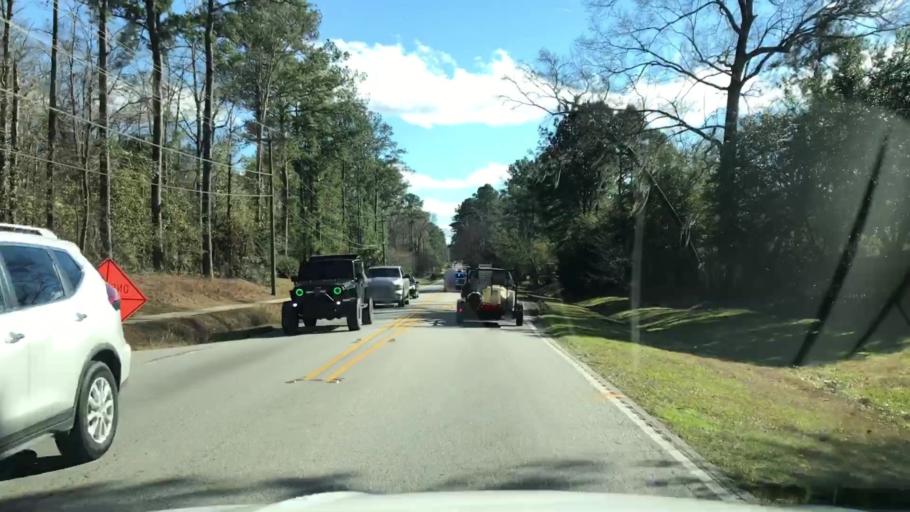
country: US
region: South Carolina
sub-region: Dorchester County
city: Summerville
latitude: 33.0309
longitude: -80.2451
